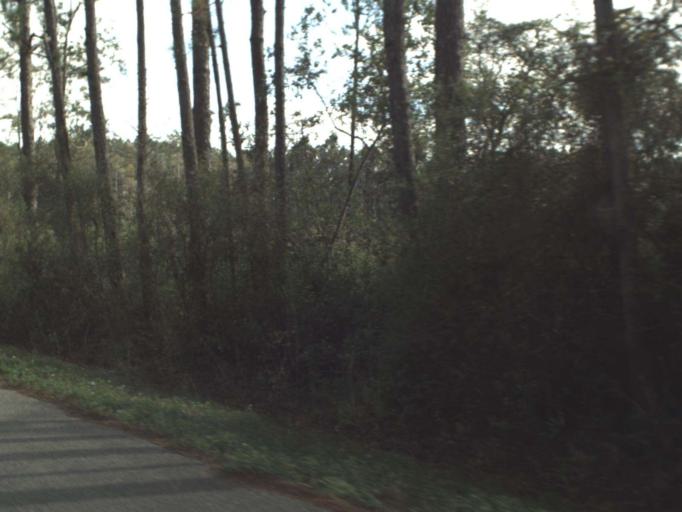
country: US
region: Florida
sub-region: Calhoun County
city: Blountstown
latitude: 30.4767
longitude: -85.0980
